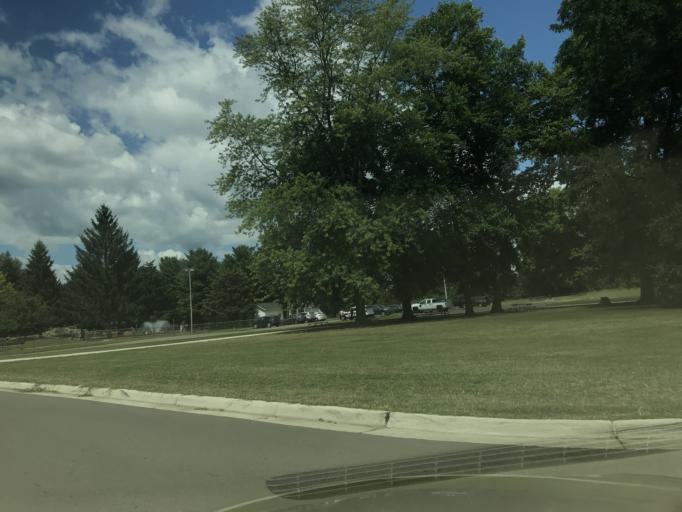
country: US
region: Michigan
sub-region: Jackson County
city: Jackson
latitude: 42.2169
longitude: -84.4157
